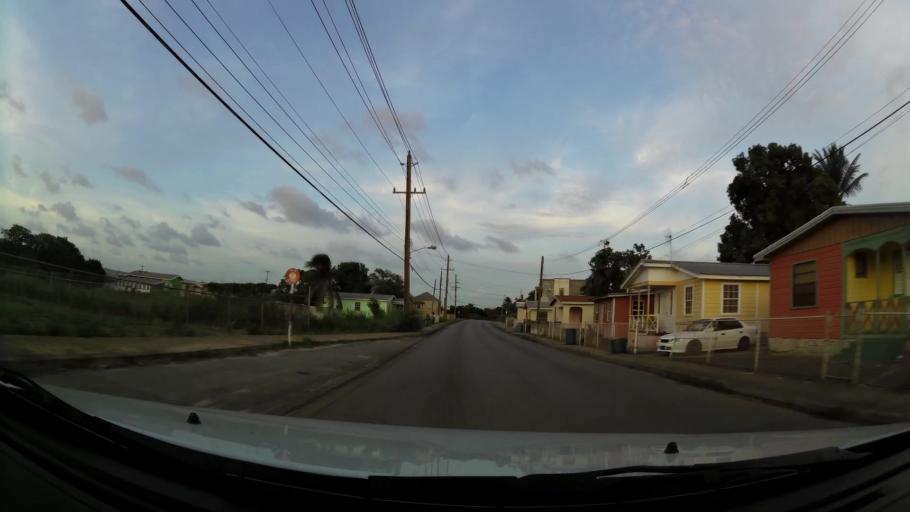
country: BB
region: Saint Philip
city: Crane
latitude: 13.1030
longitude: -59.4925
